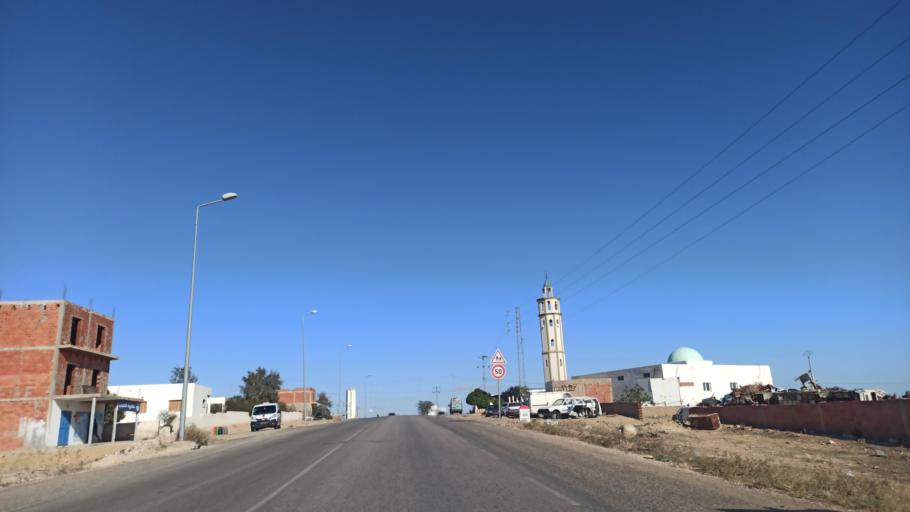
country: TN
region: Sidi Bu Zayd
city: Jilma
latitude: 35.2587
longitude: 9.4033
